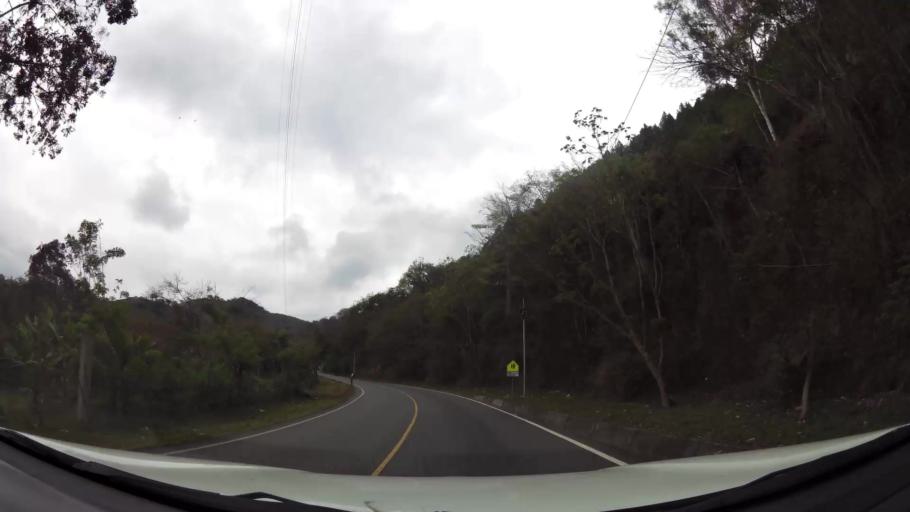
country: NI
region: Matagalpa
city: Matagalpa
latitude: 12.9708
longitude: -85.9194
